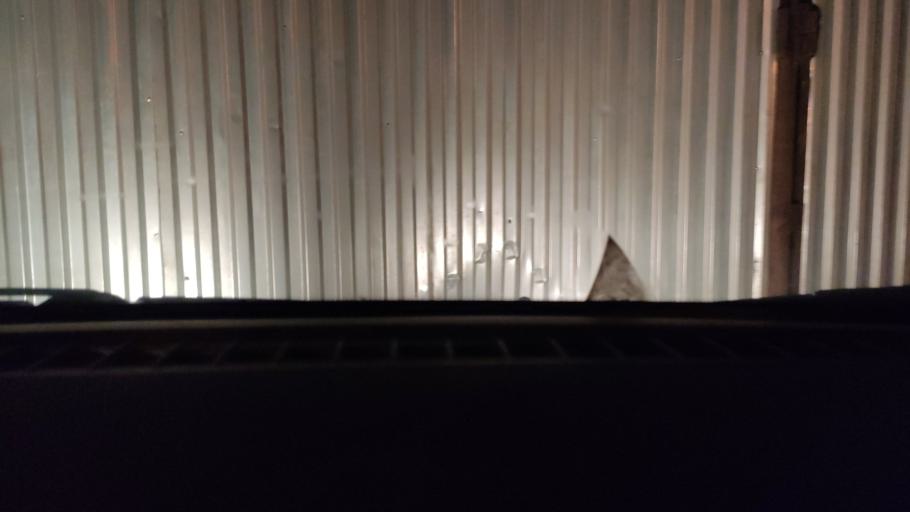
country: RU
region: Perm
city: Perm
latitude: 58.0598
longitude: 56.3359
